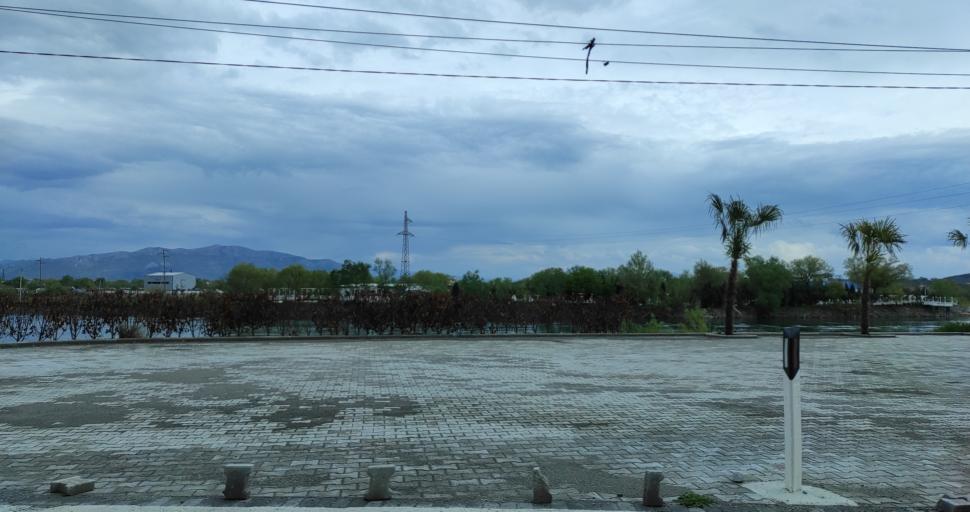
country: AL
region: Shkoder
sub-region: Rrethi i Shkodres
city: Berdica e Madhe
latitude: 42.0411
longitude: 19.4820
